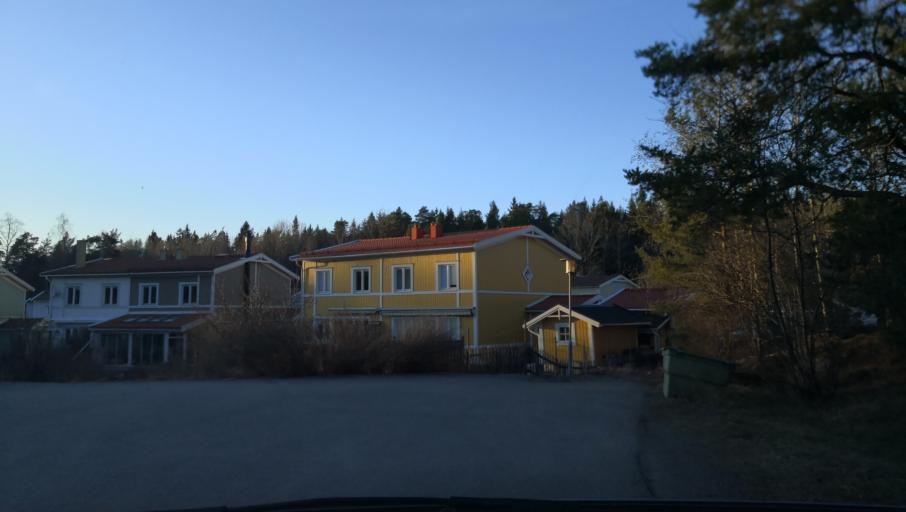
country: SE
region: Stockholm
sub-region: Varmdo Kommun
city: Gustavsberg
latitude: 59.3333
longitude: 18.4028
